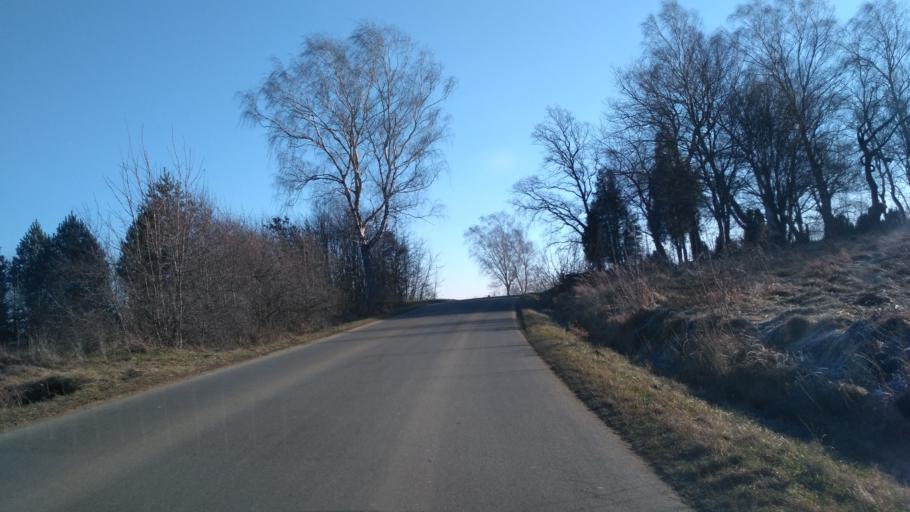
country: PL
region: Subcarpathian Voivodeship
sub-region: Powiat krosnienski
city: Rymanow
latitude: 49.5717
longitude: 21.8789
